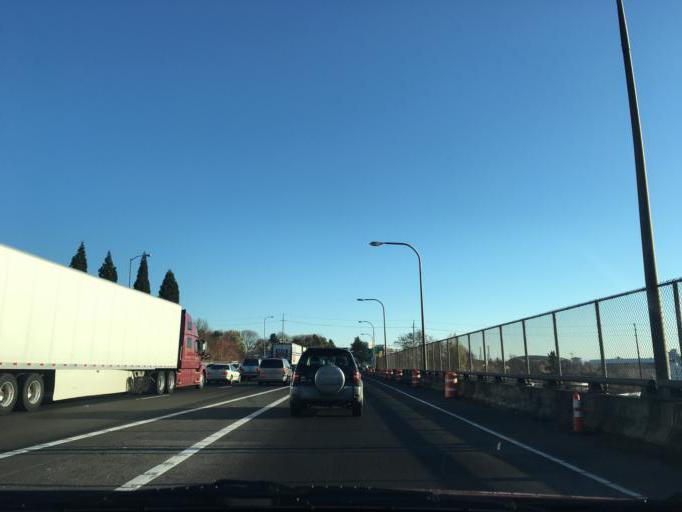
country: US
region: Oregon
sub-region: Multnomah County
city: Portland
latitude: 45.5425
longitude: -122.6738
